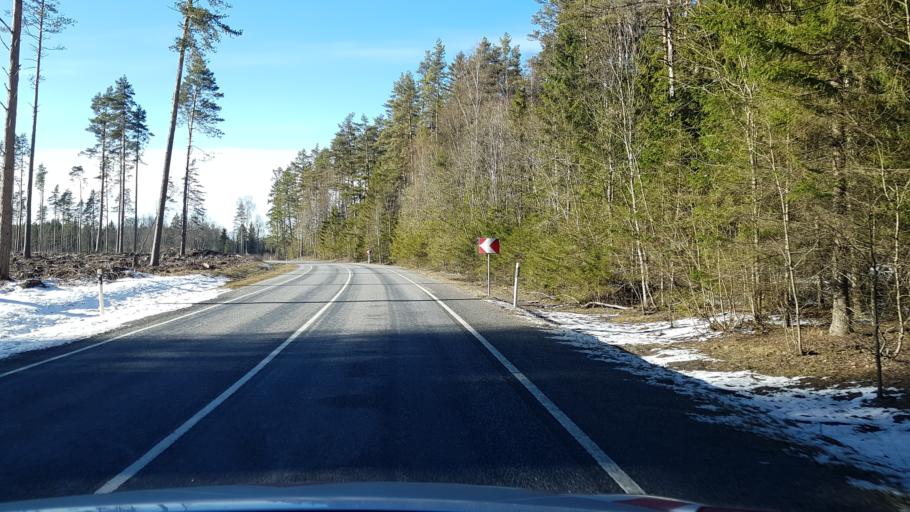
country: EE
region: Laeaene-Virumaa
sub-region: Tapa vald
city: Tapa
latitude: 59.4225
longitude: 25.9901
